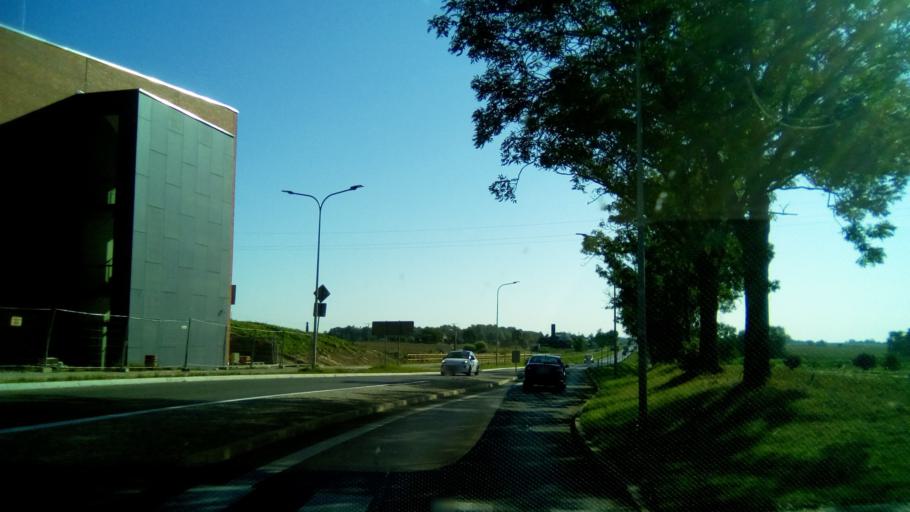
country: PL
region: Kujawsko-Pomorskie
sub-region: Powiat wloclawski
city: Brzesc Kujawski
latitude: 52.6117
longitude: 18.9025
